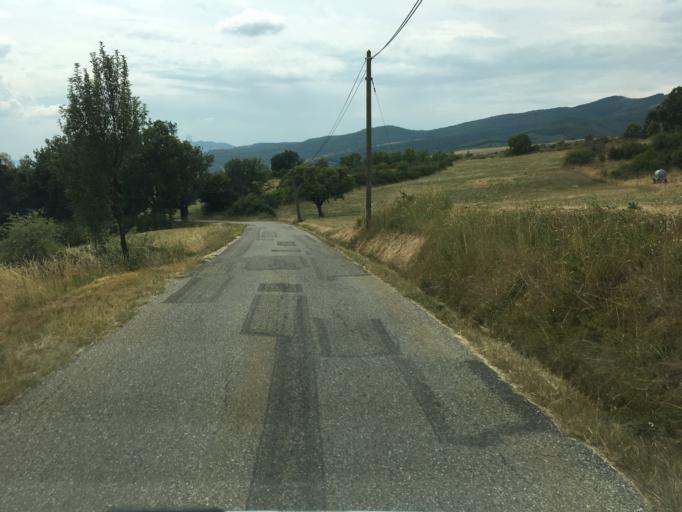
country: FR
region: Provence-Alpes-Cote d'Azur
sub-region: Departement des Alpes-de-Haute-Provence
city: Digne-les-Bains
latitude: 44.1908
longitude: 6.1421
